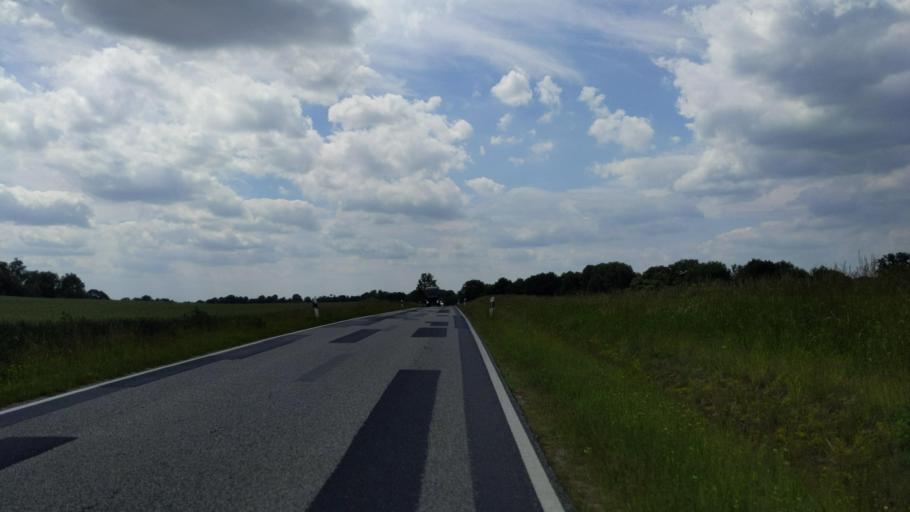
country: DE
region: Mecklenburg-Vorpommern
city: Selmsdorf
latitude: 53.8616
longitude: 10.8203
